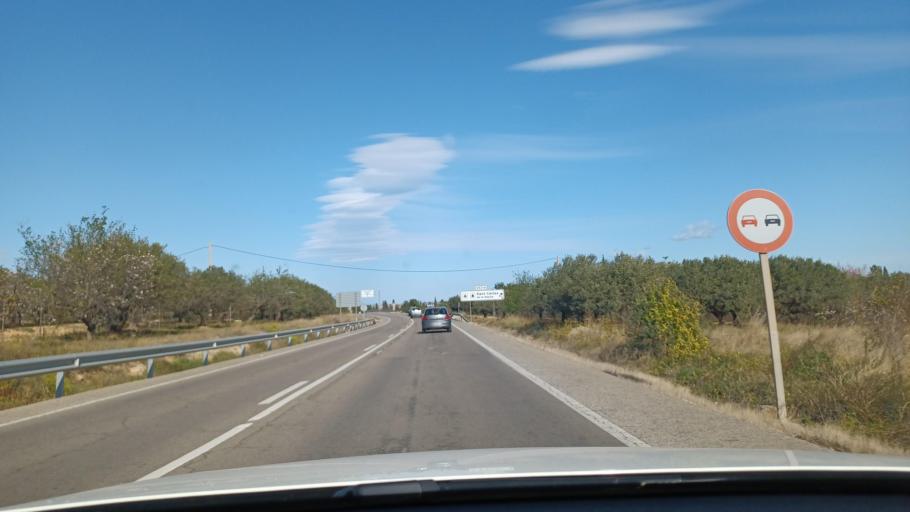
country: ES
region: Catalonia
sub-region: Provincia de Tarragona
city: Sant Carles de la Rapita
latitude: 40.6380
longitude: 0.5908
